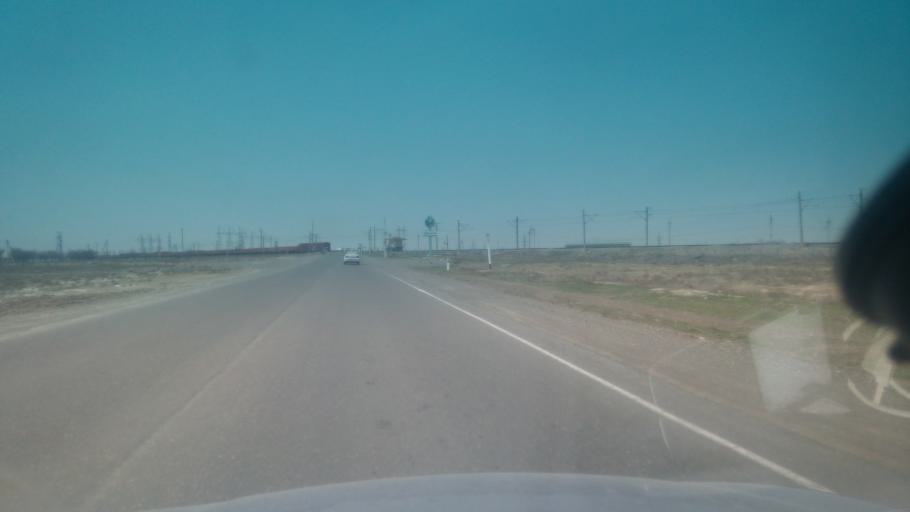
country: UZ
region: Jizzax
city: Dashtobod
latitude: 40.1514
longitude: 68.5404
